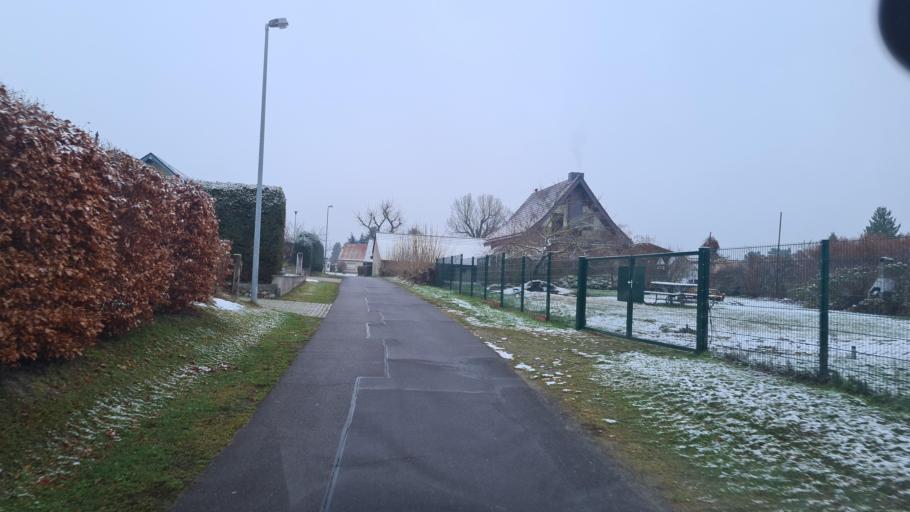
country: DE
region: Brandenburg
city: Munchehofe
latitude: 52.1584
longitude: 13.8741
